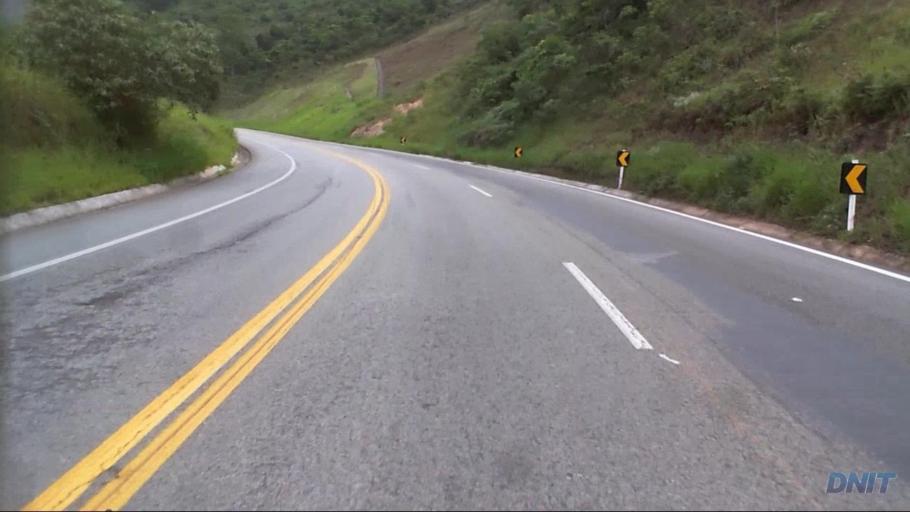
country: BR
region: Minas Gerais
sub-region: Nova Era
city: Nova Era
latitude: -19.6315
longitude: -42.8955
